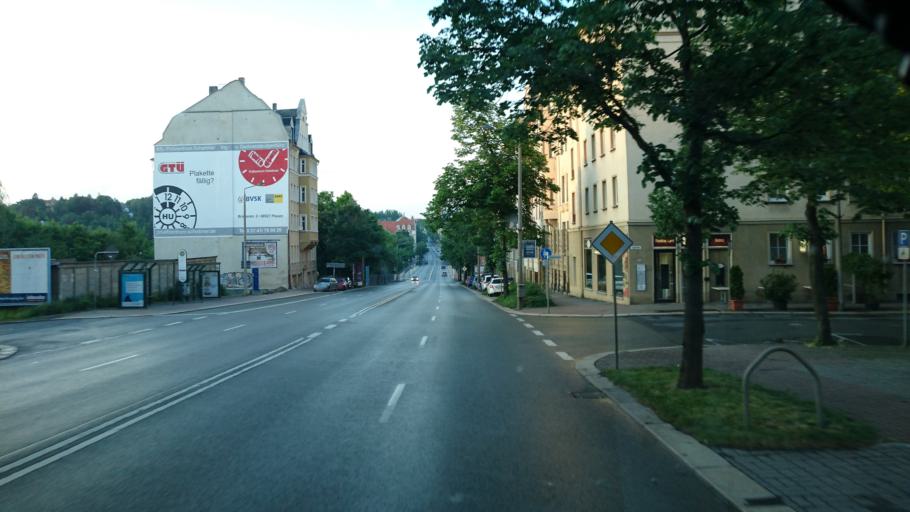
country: DE
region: Saxony
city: Plauen
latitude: 50.4968
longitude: 12.1245
